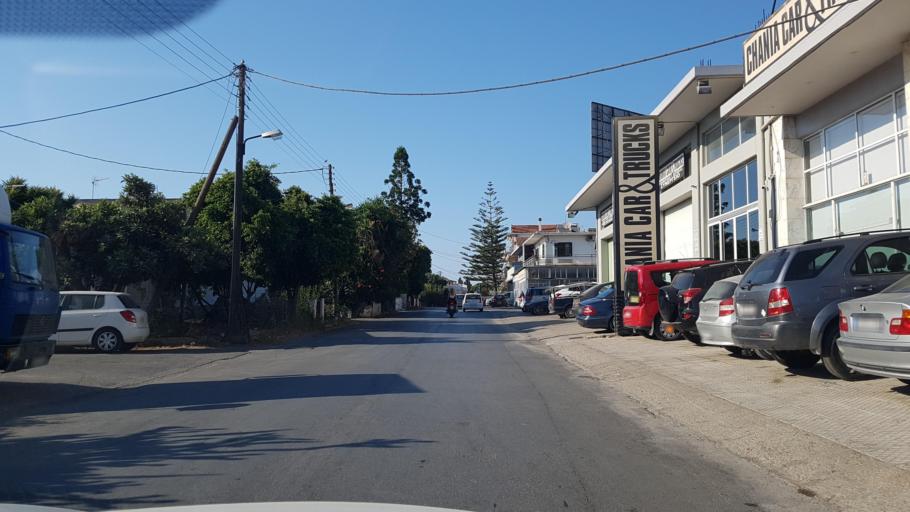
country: GR
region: Crete
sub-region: Nomos Chanias
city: Chania
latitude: 35.5017
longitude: 24.0191
